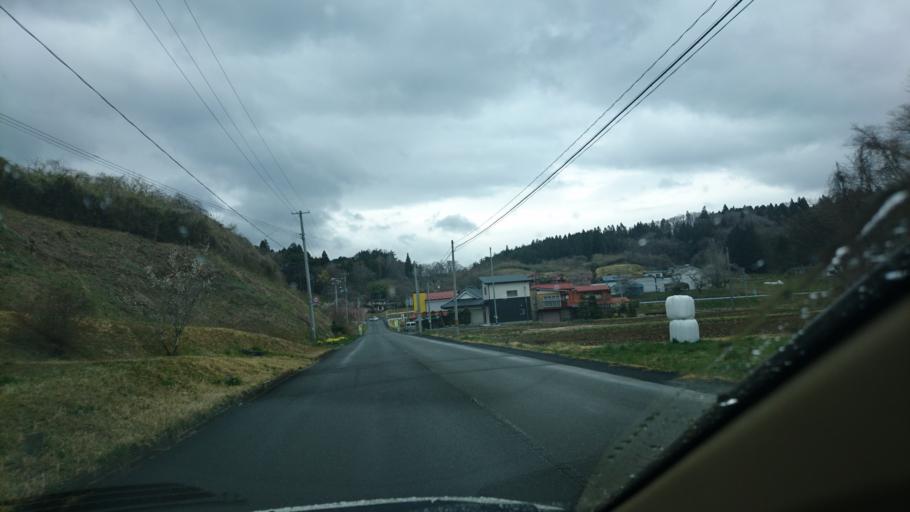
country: JP
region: Iwate
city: Ichinoseki
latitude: 38.9440
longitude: 141.3194
